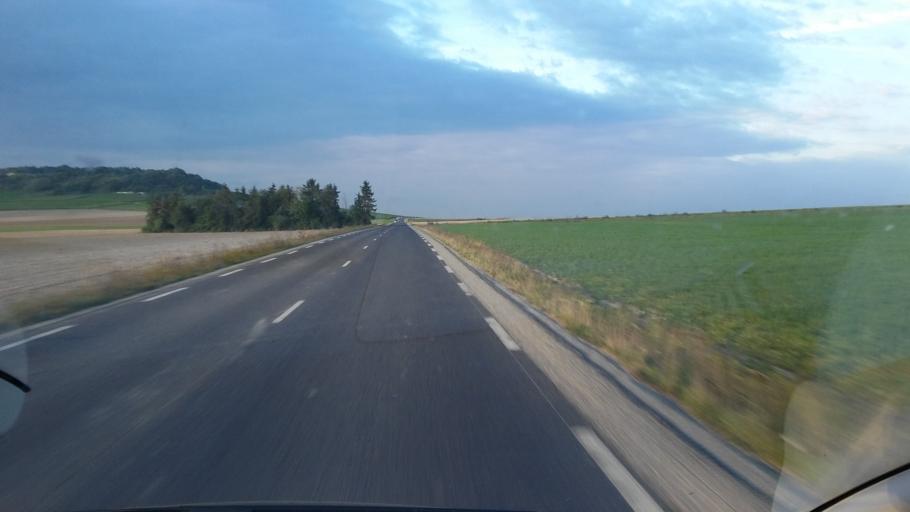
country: FR
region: Champagne-Ardenne
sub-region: Departement de la Marne
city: Vertus
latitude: 48.8479
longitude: 4.0007
